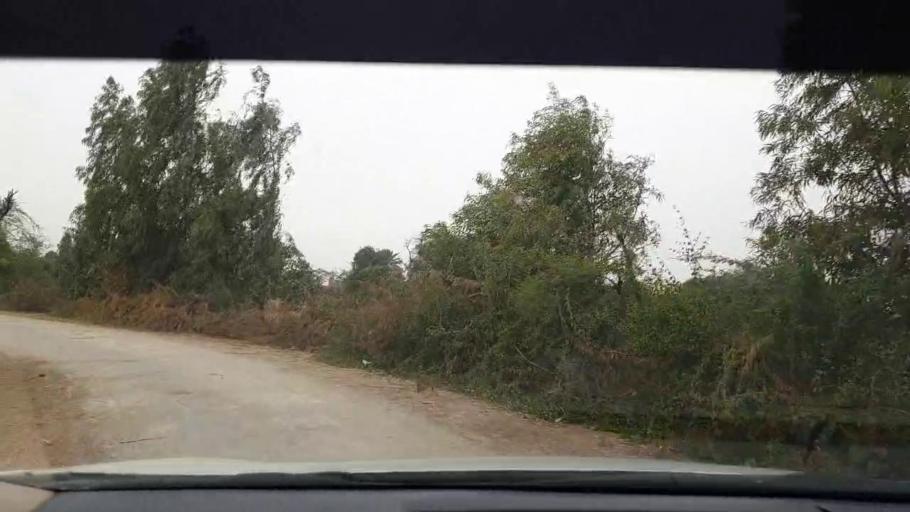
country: PK
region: Sindh
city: Berani
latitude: 25.8745
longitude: 68.7964
